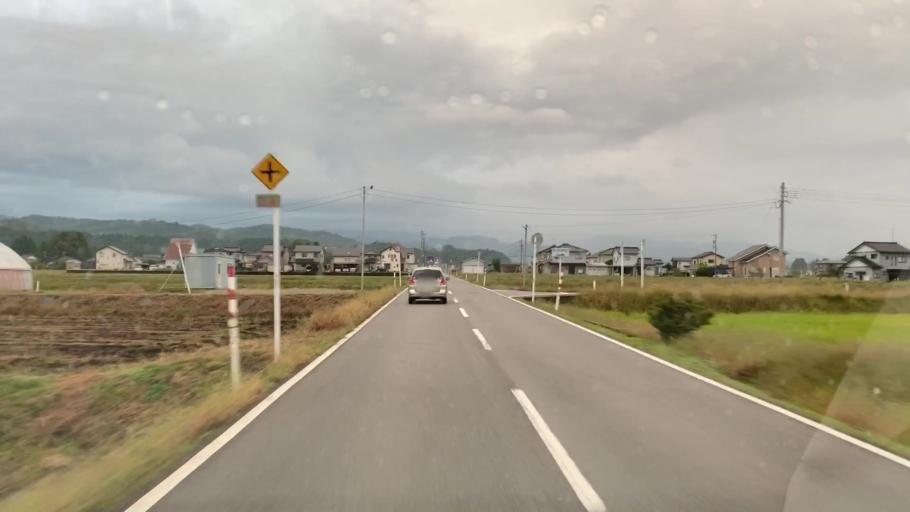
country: JP
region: Toyama
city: Kamiichi
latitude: 36.6332
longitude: 137.3286
